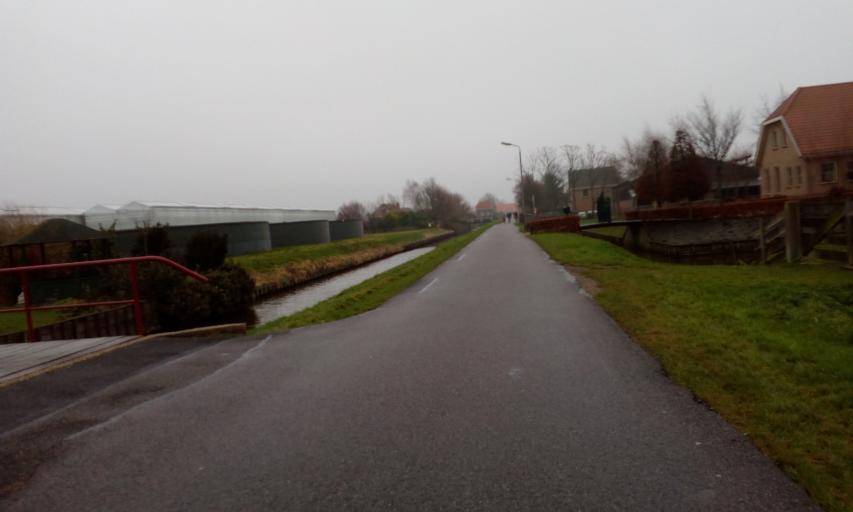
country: NL
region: South Holland
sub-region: Gemeente Pijnacker-Nootdorp
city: Pijnacker
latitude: 52.0210
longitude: 4.4183
